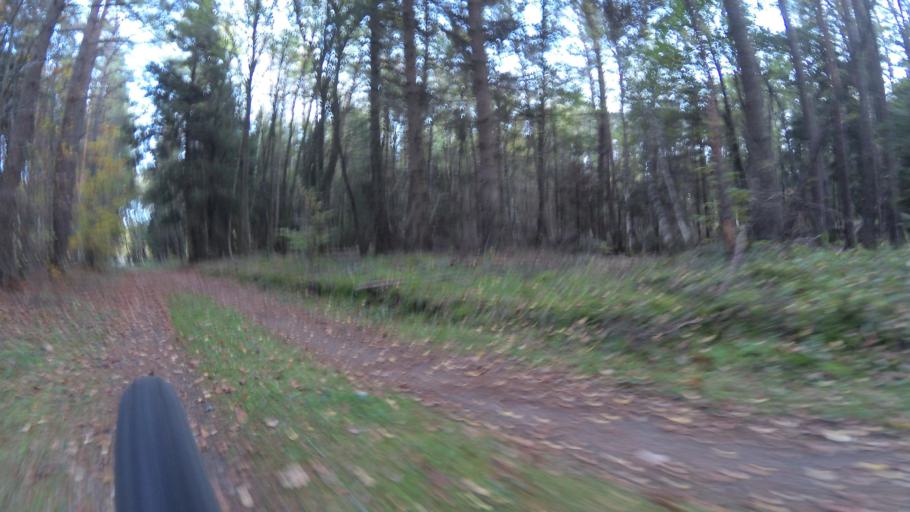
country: DE
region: Rheinland-Pfalz
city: Steinwenden
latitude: 49.4211
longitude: 7.5285
